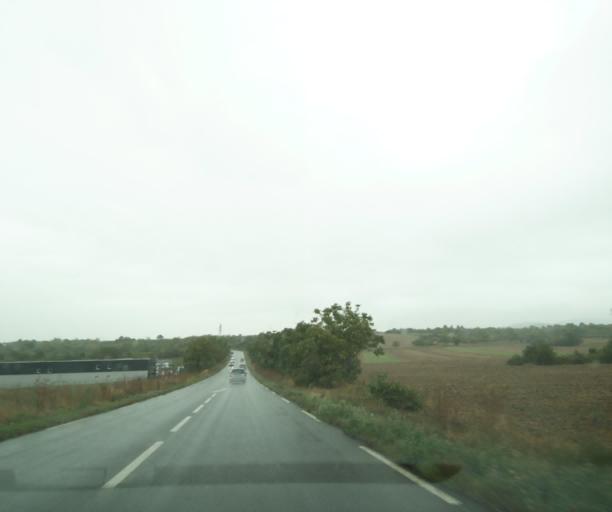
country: FR
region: Auvergne
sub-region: Departement du Puy-de-Dome
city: Cebazat
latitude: 45.8469
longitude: 3.1050
